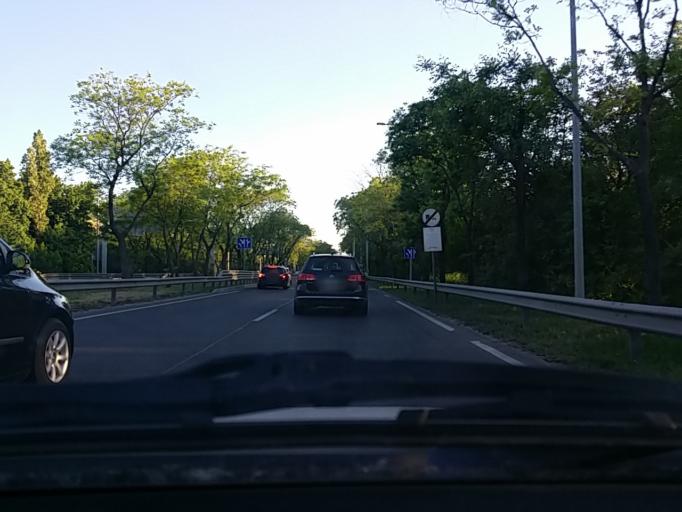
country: HU
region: Pest
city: Budakalasz
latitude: 47.6065
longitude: 19.0608
